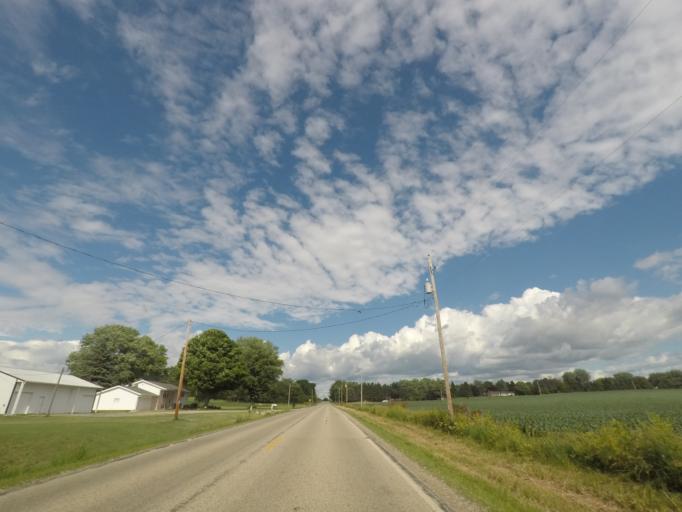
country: US
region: Wisconsin
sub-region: Rock County
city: Janesville
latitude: 42.7010
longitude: -89.0752
